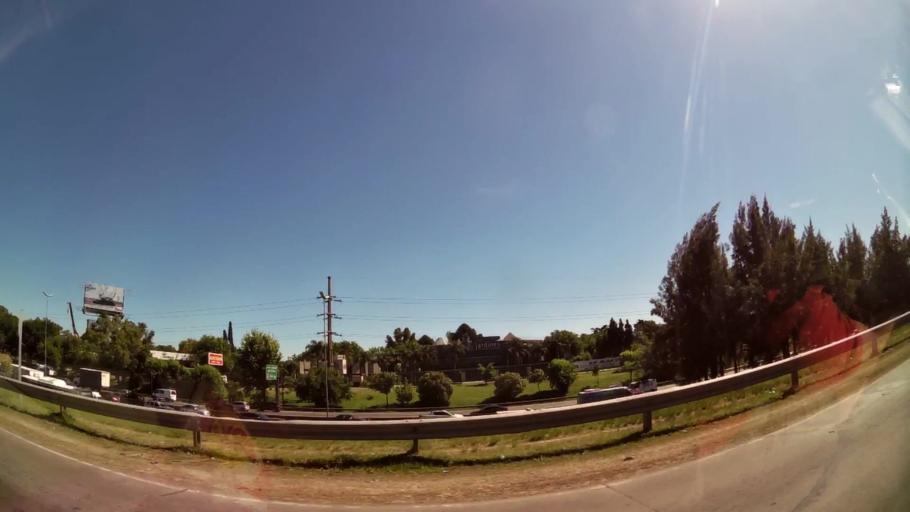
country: AR
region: Buenos Aires
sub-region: Partido de Tigre
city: Tigre
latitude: -34.4847
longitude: -58.6227
